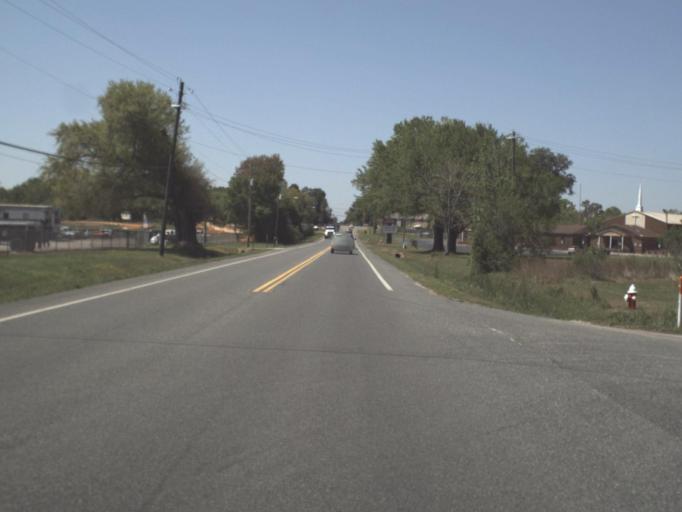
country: US
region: Florida
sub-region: Escambia County
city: Bellview
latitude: 30.4807
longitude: -87.3107
